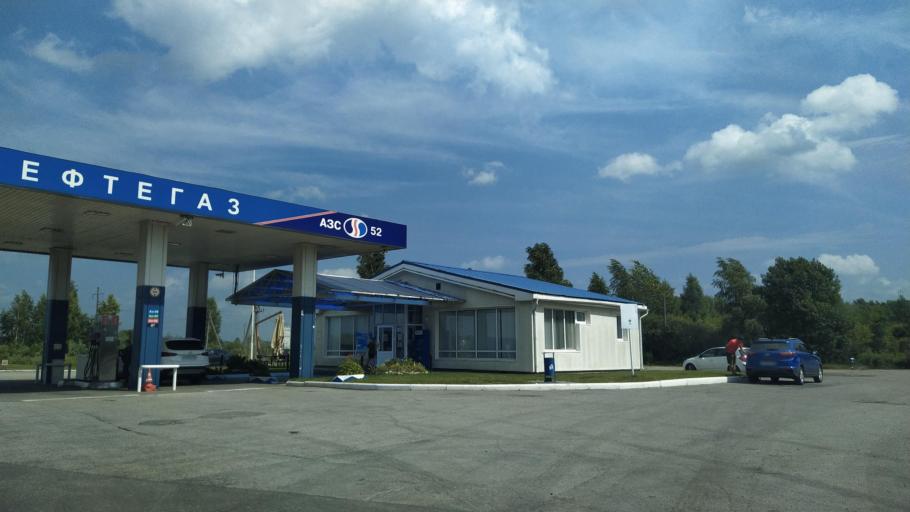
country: RU
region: Pskov
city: Ostrov
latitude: 57.3319
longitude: 28.3701
